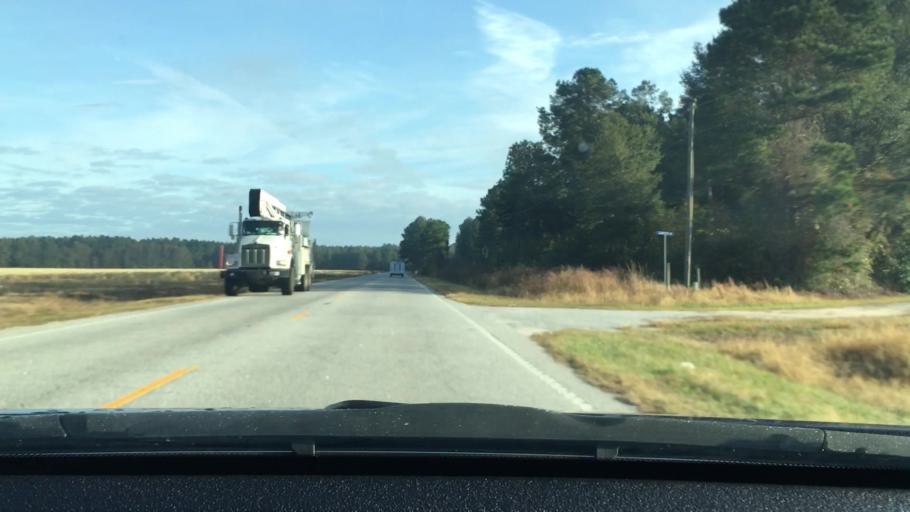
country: US
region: South Carolina
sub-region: Sumter County
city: East Sumter
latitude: 34.0262
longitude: -80.2757
